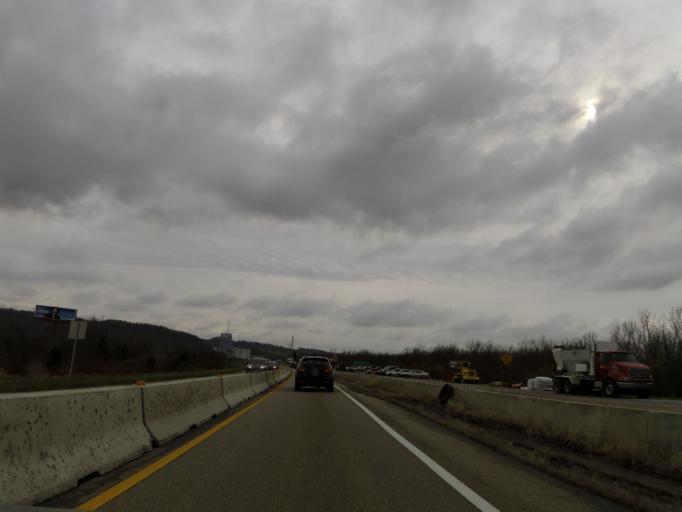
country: US
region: Indiana
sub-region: Dearborn County
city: Lawrenceburg
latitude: 39.1121
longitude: -84.8324
